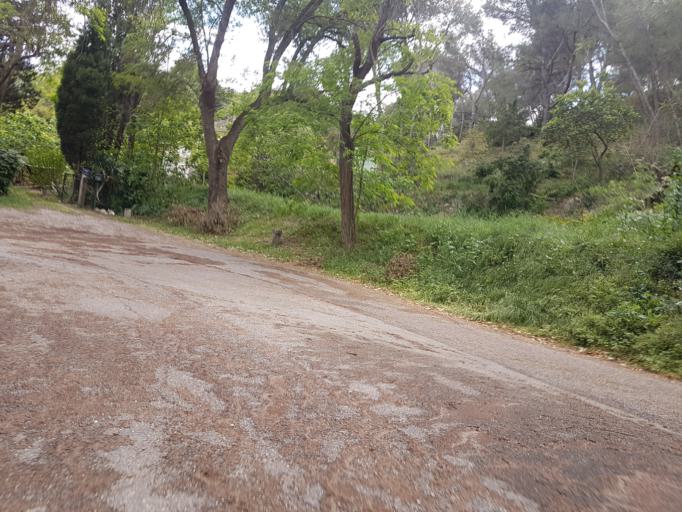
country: FR
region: Languedoc-Roussillon
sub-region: Departement du Gard
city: Beaucaire
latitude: 43.8229
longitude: 4.6275
